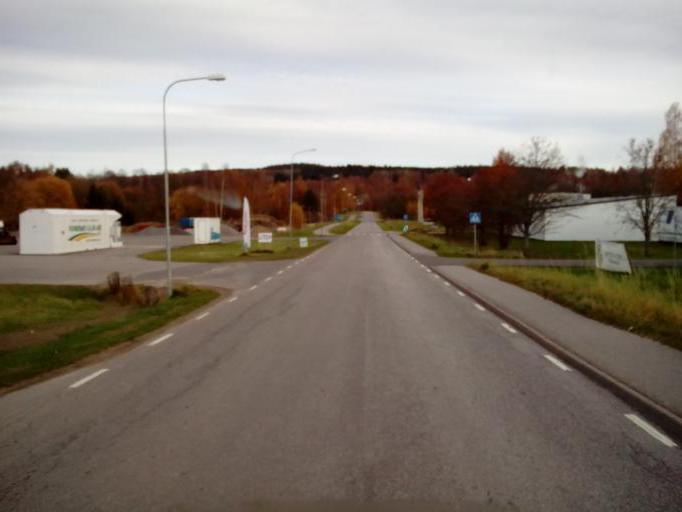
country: SE
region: OEstergoetland
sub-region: Kinda Kommun
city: Kisa
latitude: 57.9853
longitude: 15.6503
